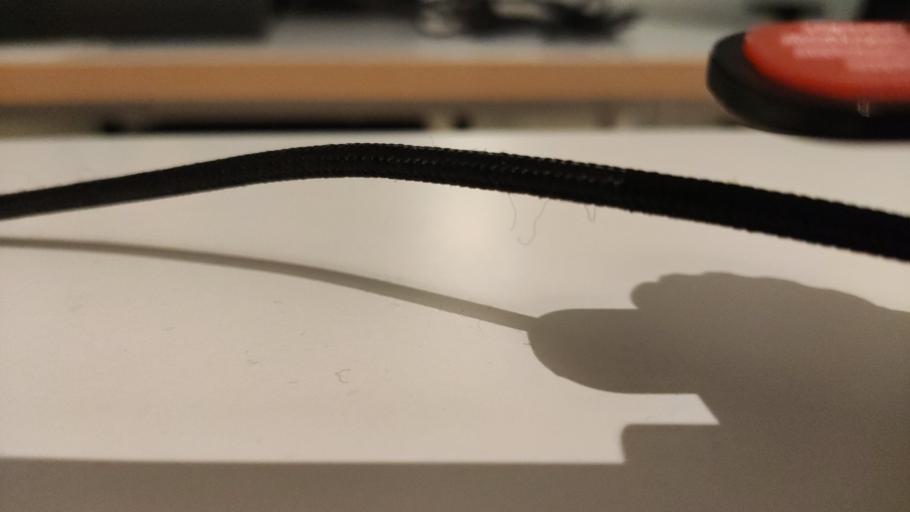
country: RU
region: Moskovskaya
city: Novosin'kovo
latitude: 56.3955
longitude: 37.2760
